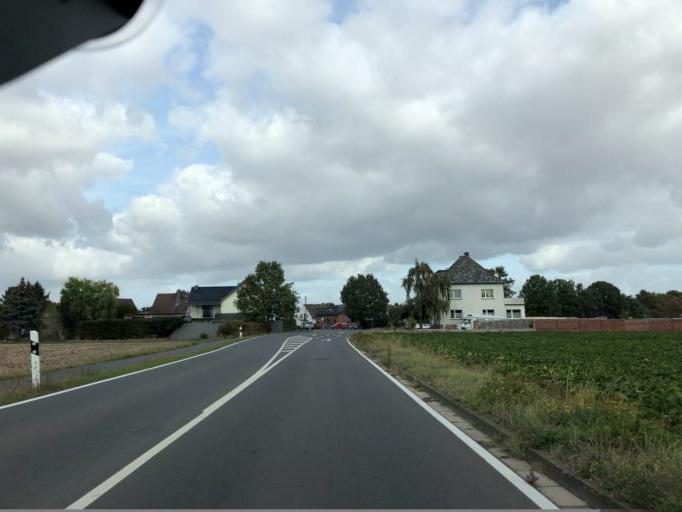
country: DE
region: North Rhine-Westphalia
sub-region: Regierungsbezirk Koln
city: Rheinbach
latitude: 50.6479
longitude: 6.9191
